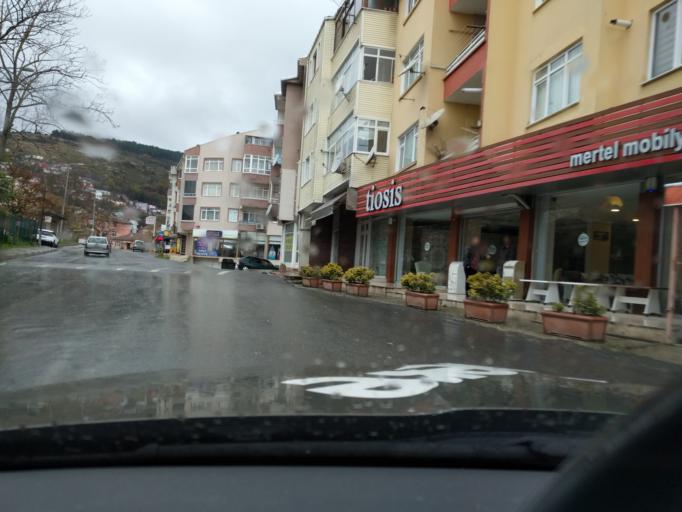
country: TR
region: Istanbul
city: Catalca
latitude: 41.1461
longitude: 28.4582
